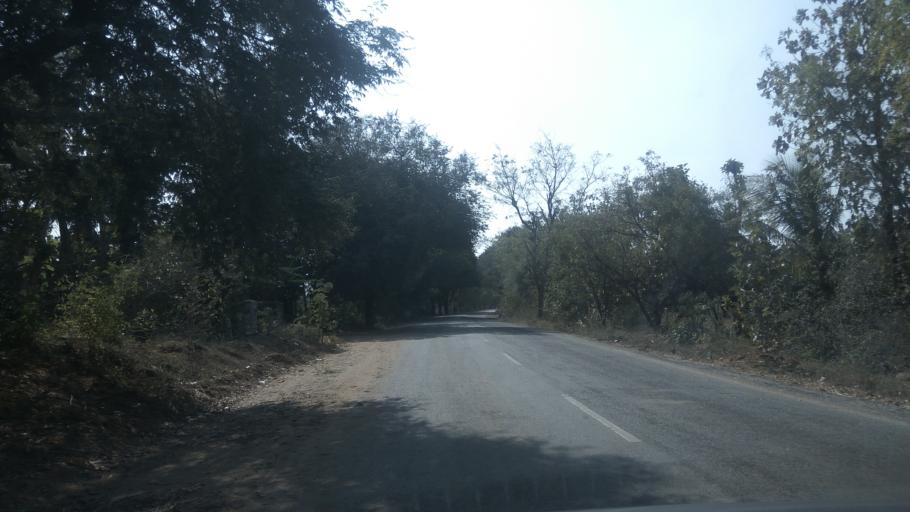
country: IN
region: Andhra Pradesh
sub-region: Chittoor
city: Renigunta
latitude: 13.5533
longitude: 79.4944
